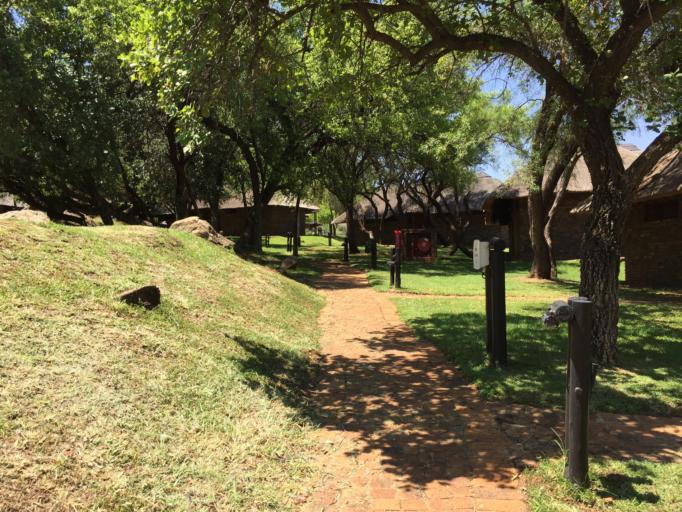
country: ZA
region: North-West
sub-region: Bojanala Platinum District Municipality
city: Mogwase
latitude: -25.3424
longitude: 27.0569
